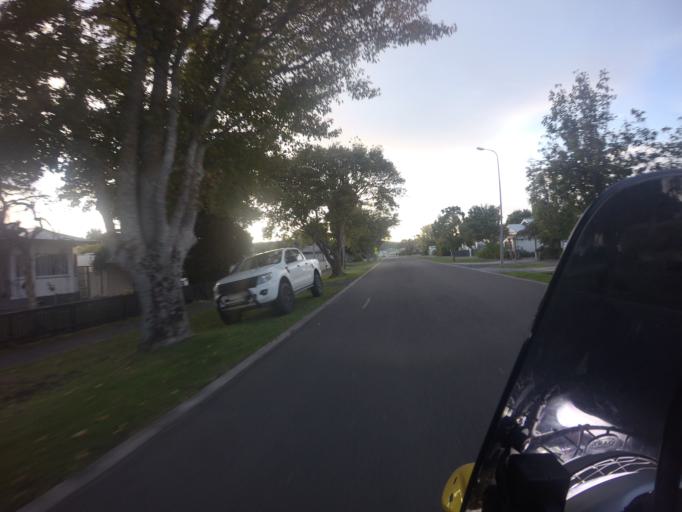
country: NZ
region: Gisborne
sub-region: Gisborne District
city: Gisborne
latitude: -38.6695
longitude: 178.0420
